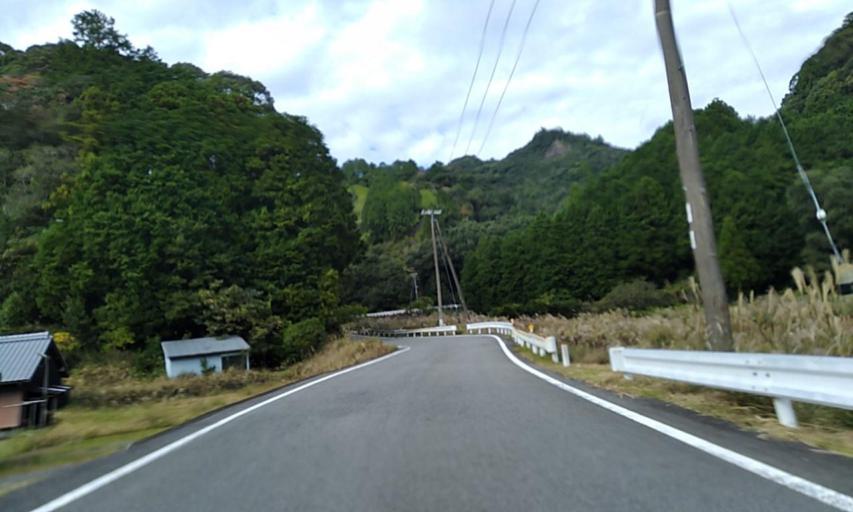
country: JP
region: Wakayama
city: Shingu
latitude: 33.5408
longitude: 135.8304
